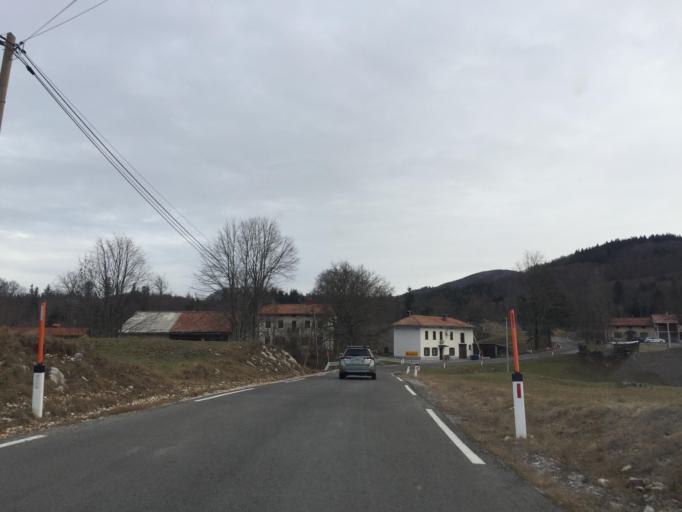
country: SI
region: Nova Gorica
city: Sempas
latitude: 45.9898
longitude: 13.7694
